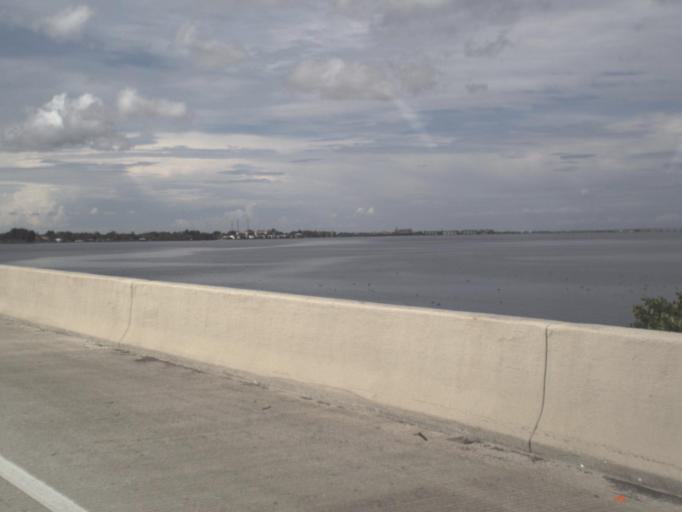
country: US
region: Florida
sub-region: Charlotte County
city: Harbour Heights
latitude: 26.9647
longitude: -82.0199
